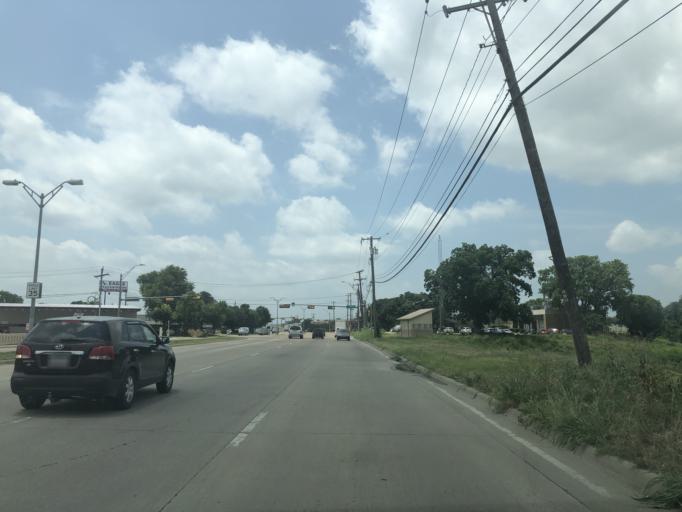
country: US
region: Texas
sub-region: Dallas County
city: Dallas
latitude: 32.8083
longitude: -96.8514
